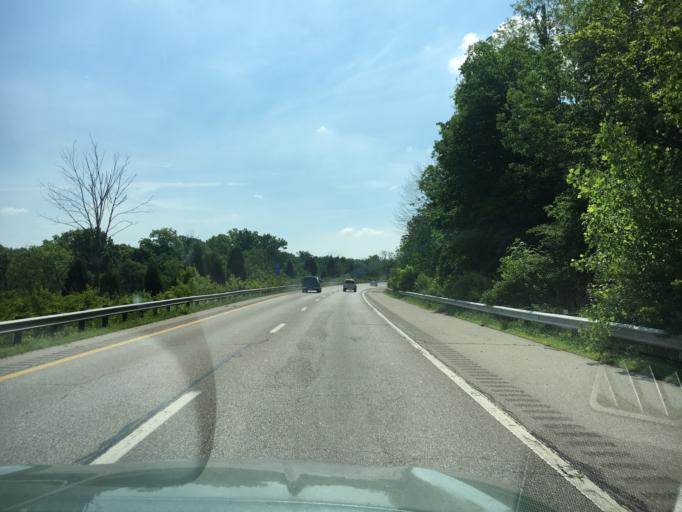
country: US
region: Ohio
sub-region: Hamilton County
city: Dent
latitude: 39.1958
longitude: -84.6537
